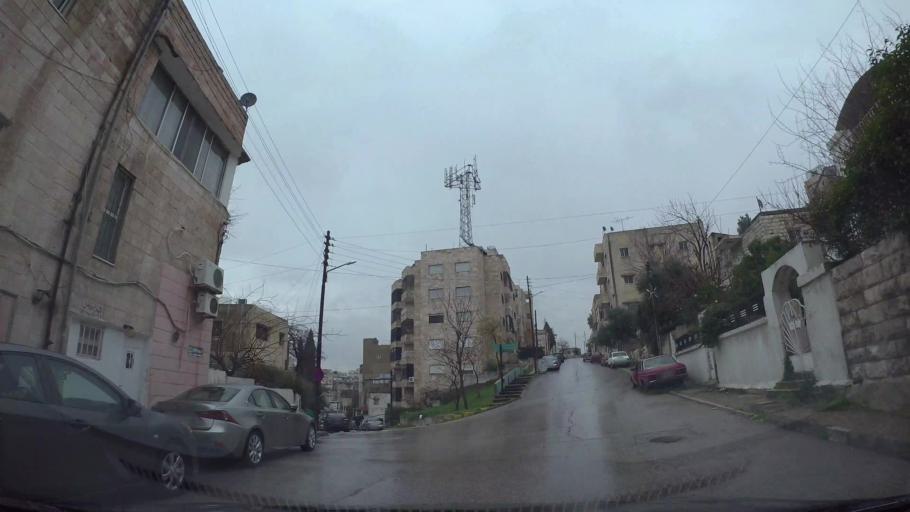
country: JO
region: Amman
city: Amman
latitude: 31.9577
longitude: 35.9256
